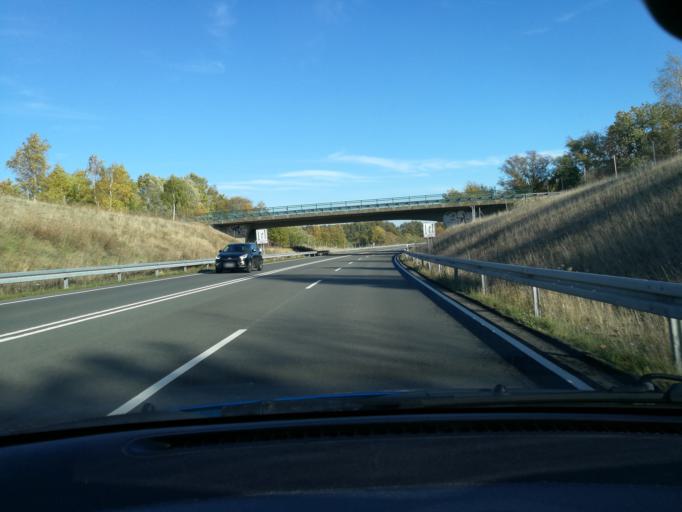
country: DE
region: Lower Saxony
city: Dahlenburg
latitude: 53.1945
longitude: 10.7186
